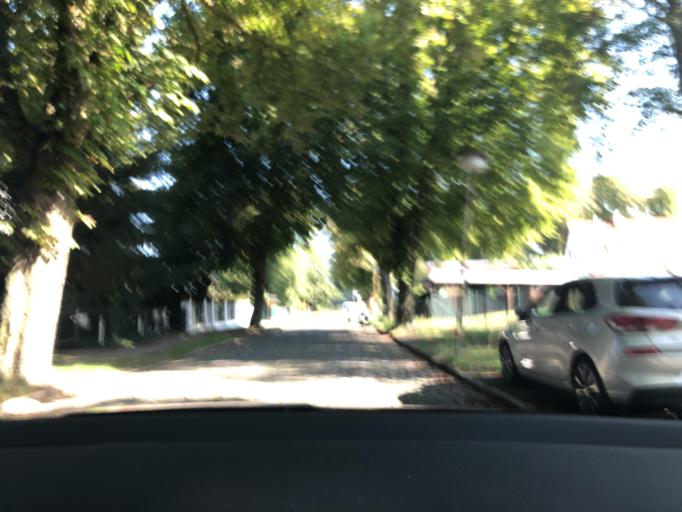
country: DE
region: Brandenburg
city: Erkner
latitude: 52.4174
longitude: 13.7368
